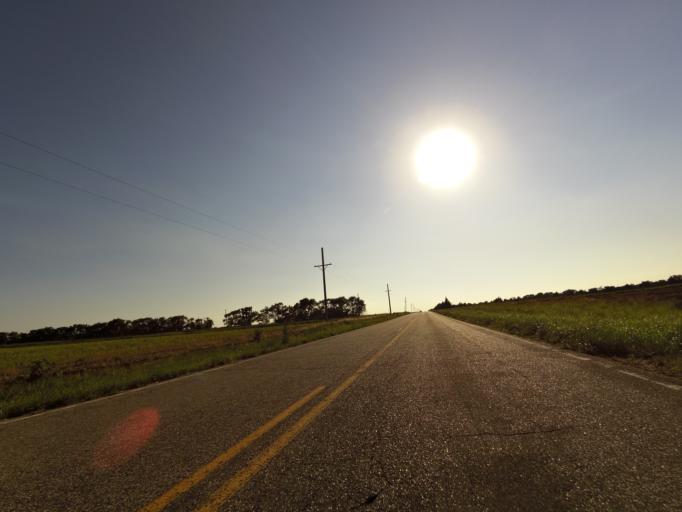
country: US
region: Kansas
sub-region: McPherson County
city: Moundridge
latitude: 38.1451
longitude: -97.5540
